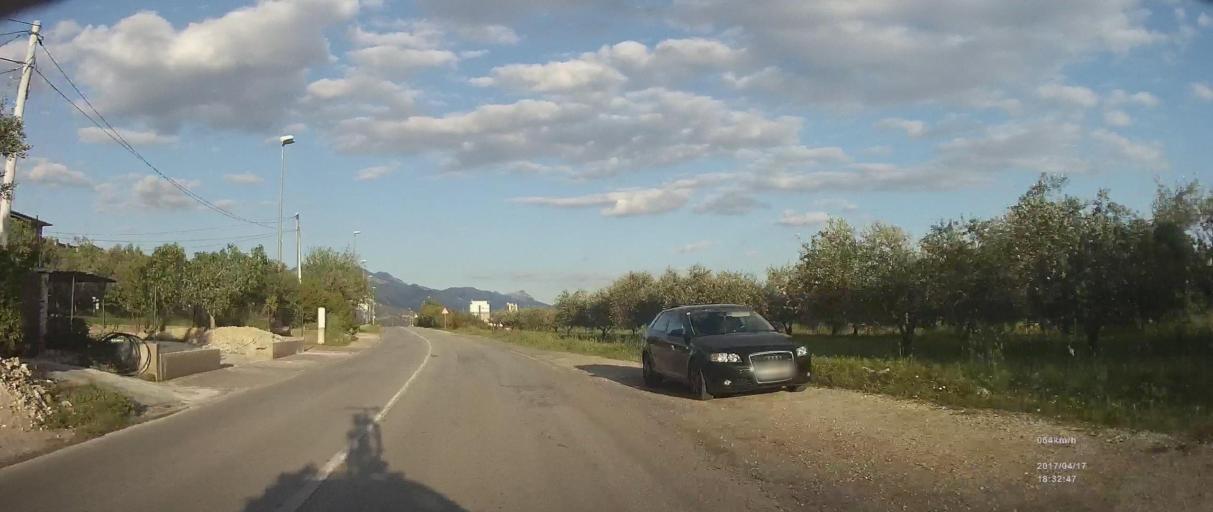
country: HR
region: Splitsko-Dalmatinska
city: Vranjic
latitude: 43.5414
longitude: 16.4505
